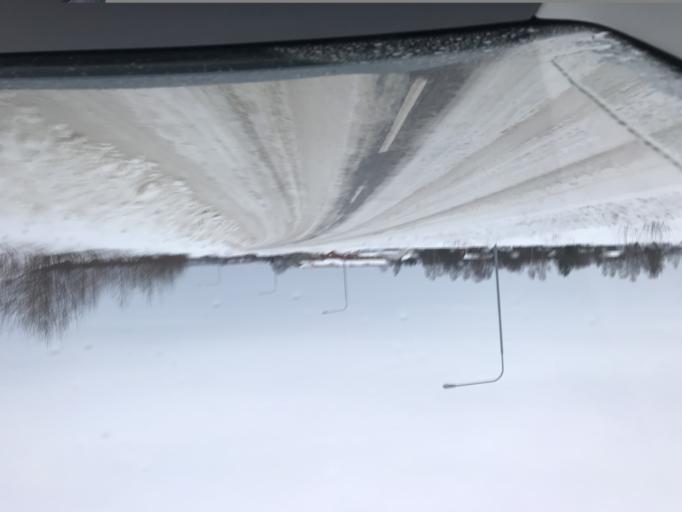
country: SE
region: Norrbotten
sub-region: Lulea Kommun
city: Sodra Sunderbyn
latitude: 65.6653
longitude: 21.9343
